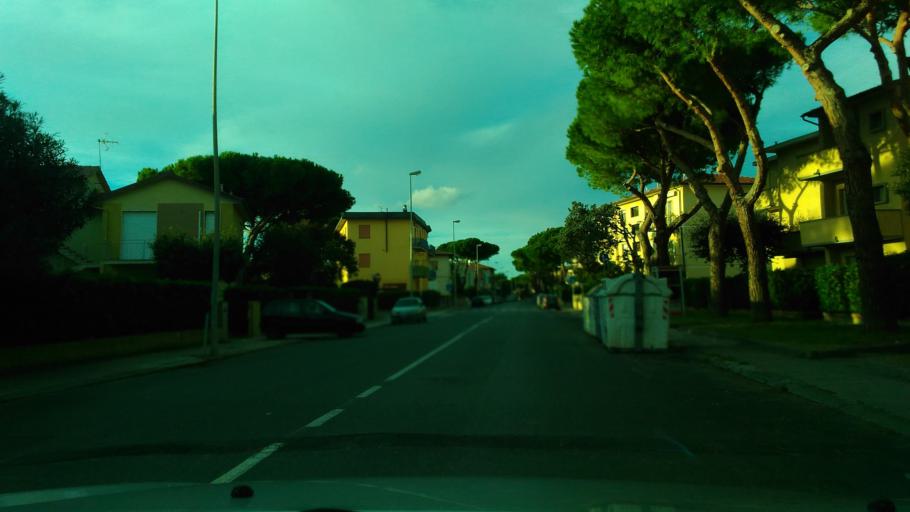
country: IT
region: Tuscany
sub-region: Provincia di Livorno
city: Cecina
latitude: 43.2983
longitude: 10.4991
